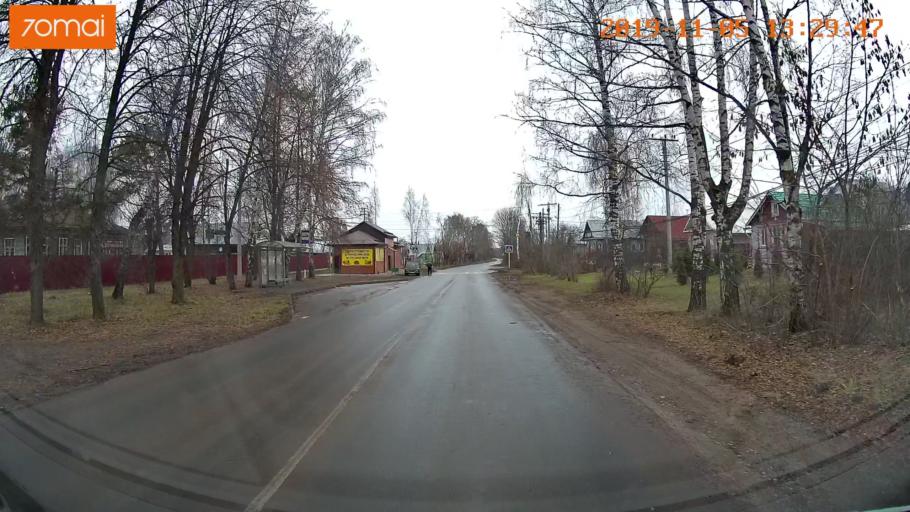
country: RU
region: Ivanovo
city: Shuya
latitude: 56.8631
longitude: 41.3971
